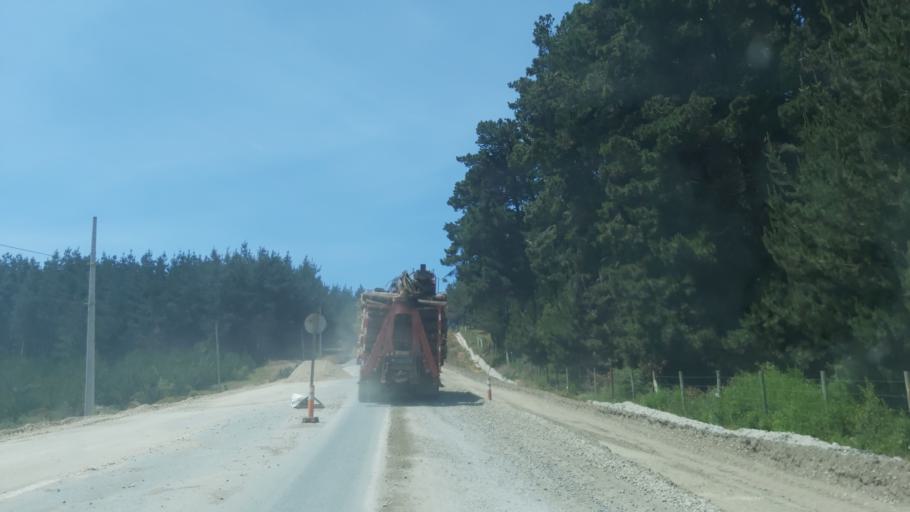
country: CL
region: Maule
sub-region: Provincia de Talca
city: Constitucion
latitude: -35.4501
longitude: -72.4777
